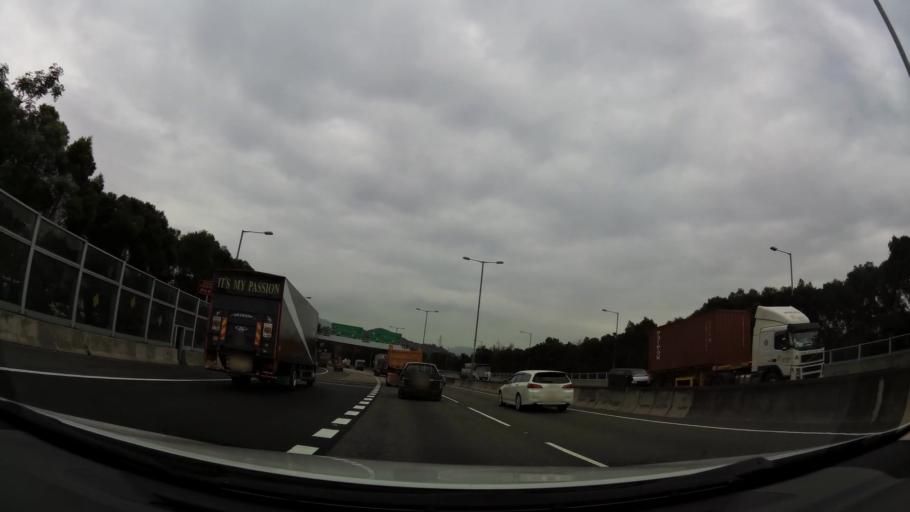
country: HK
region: Yuen Long
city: Yuen Long Kau Hui
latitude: 22.4343
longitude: 114.0325
